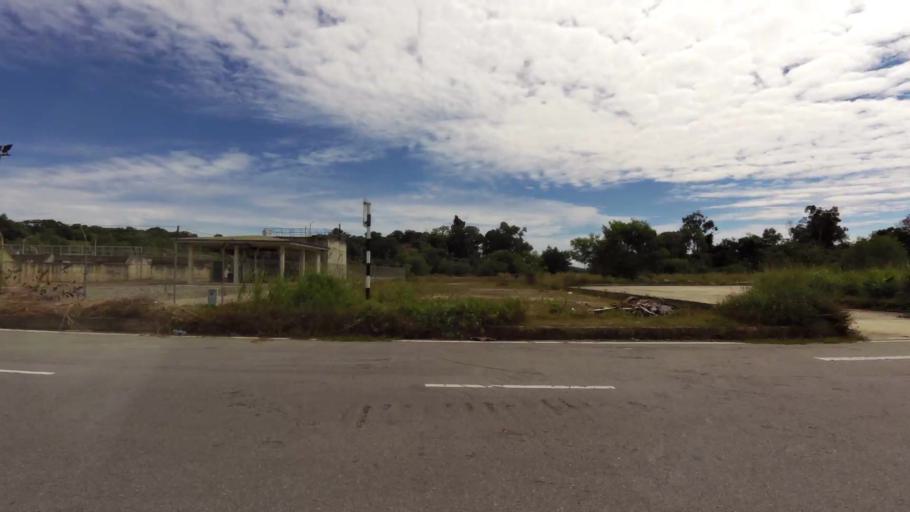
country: BN
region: Brunei and Muara
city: Bandar Seri Begawan
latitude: 4.9873
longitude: 115.0181
